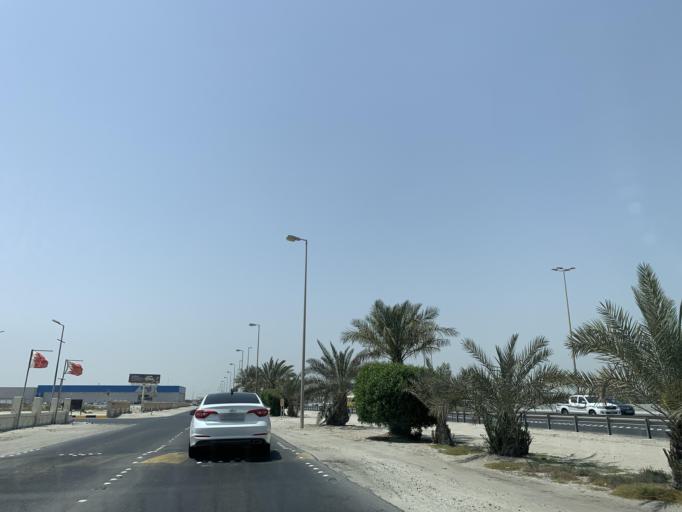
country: BH
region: Manama
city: Jidd Hafs
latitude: 26.1961
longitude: 50.5439
